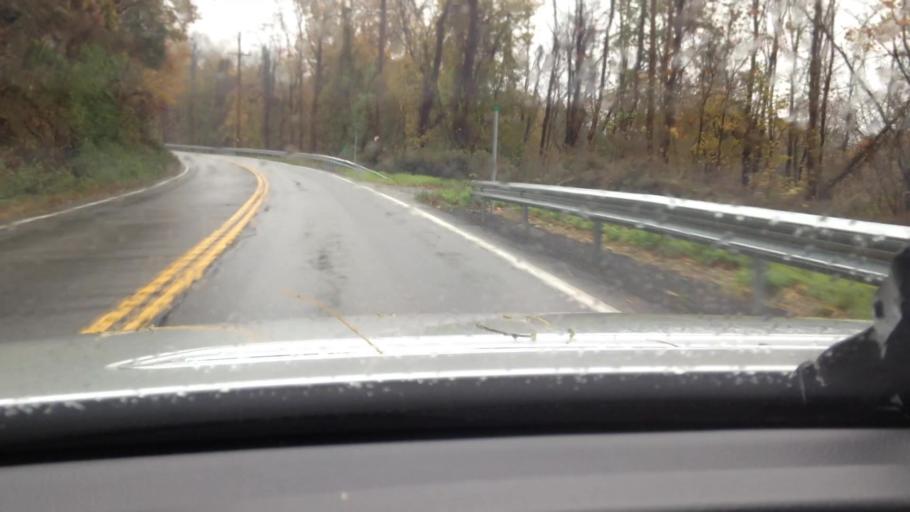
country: US
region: New York
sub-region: Dutchess County
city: Beacon
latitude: 41.4719
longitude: -73.9755
